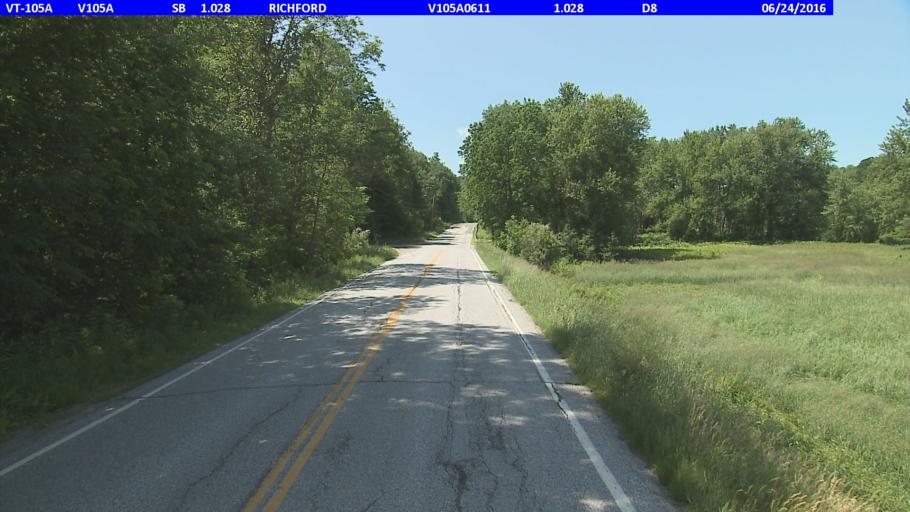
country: US
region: Vermont
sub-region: Franklin County
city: Richford
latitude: 45.0045
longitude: -72.5973
